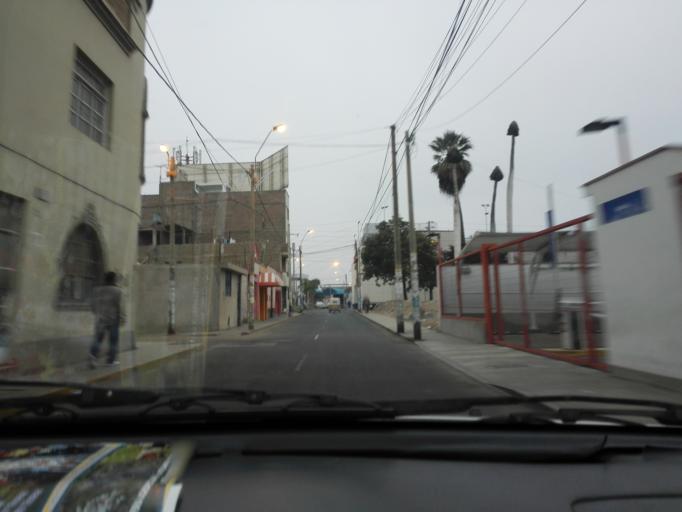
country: PE
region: Ica
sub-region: Provincia de Ica
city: Ica
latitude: -14.0696
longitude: -75.7278
